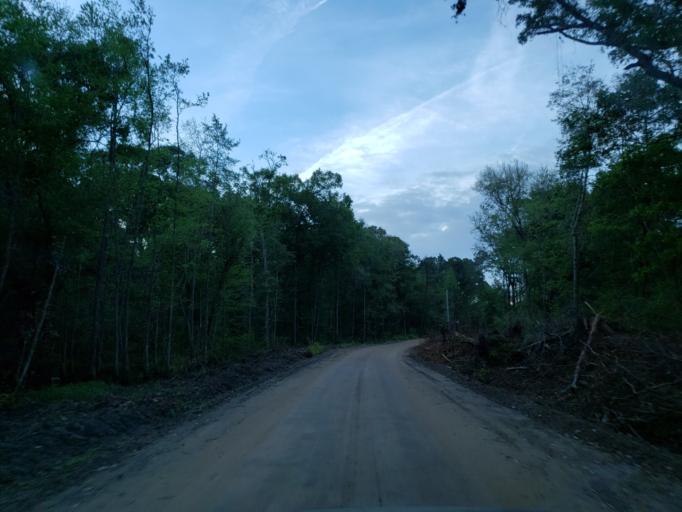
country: US
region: Georgia
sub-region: Lowndes County
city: Hahira
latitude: 30.9579
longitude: -83.3935
